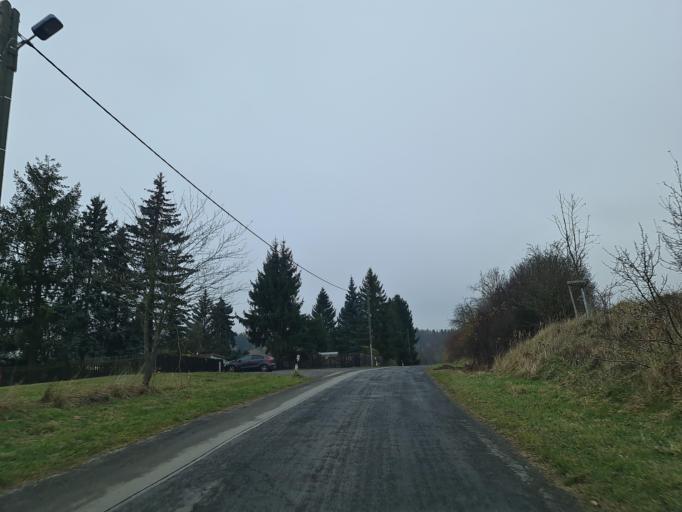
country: DE
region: Saxony
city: Mehltheuer
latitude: 50.5141
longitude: 12.0471
